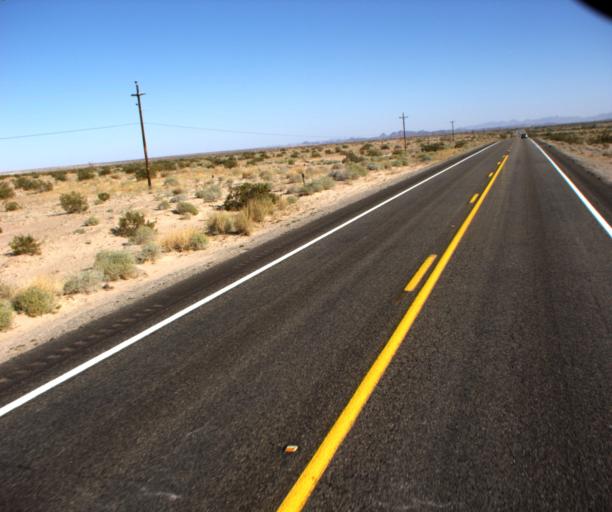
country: US
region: Arizona
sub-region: Yuma County
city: Fortuna Foothills
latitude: 32.8444
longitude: -114.3669
